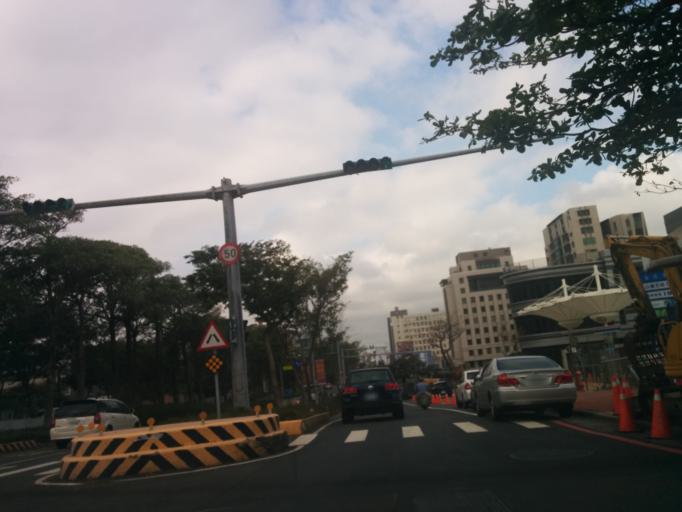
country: TW
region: Taiwan
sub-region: Hsinchu
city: Hsinchu
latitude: 24.8008
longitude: 121.0027
